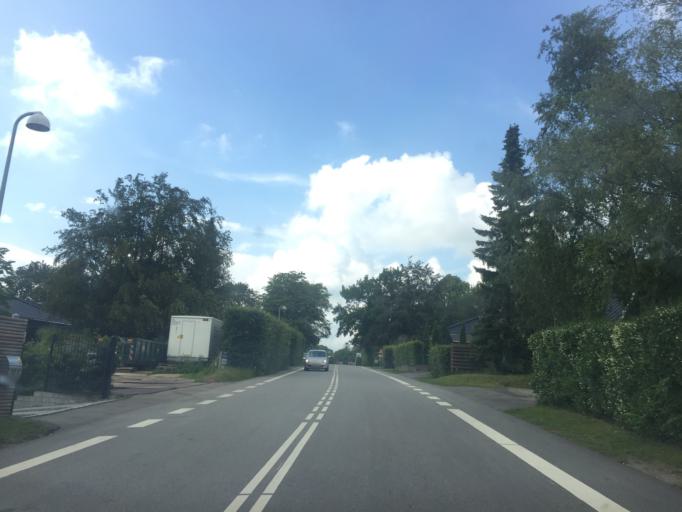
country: DK
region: Zealand
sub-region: Roskilde Kommune
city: Gundsomagle
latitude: 55.7061
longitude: 12.1625
